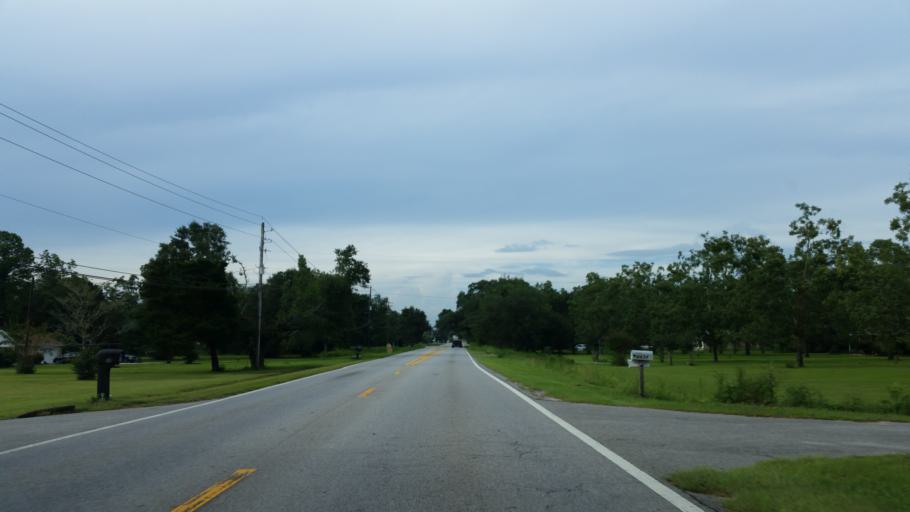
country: US
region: Florida
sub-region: Santa Rosa County
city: Pace
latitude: 30.5975
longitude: -87.1113
